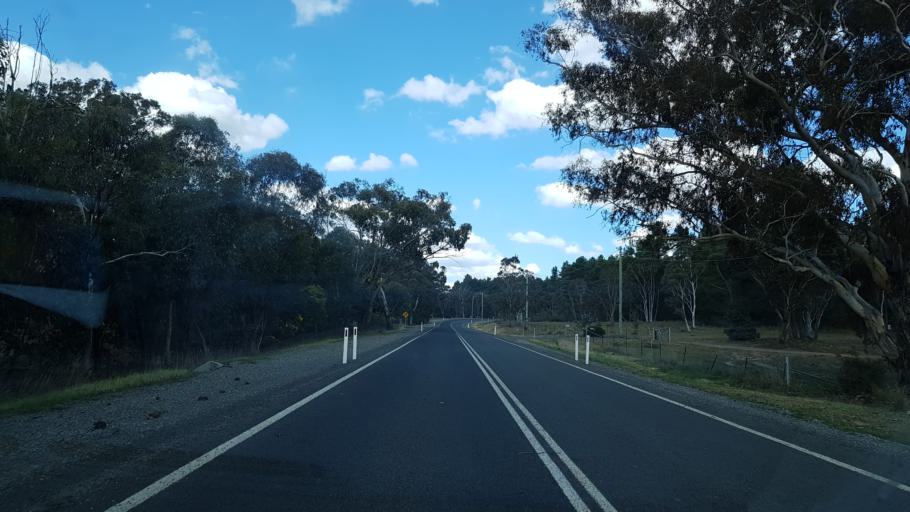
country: AU
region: New South Wales
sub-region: Queanbeyan
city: Queanbeyan
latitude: -35.3930
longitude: 149.2988
